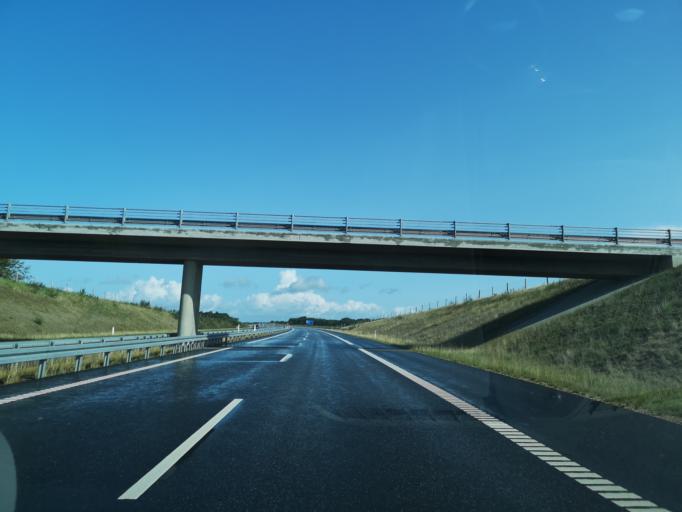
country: DK
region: Central Jutland
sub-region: Herning Kommune
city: Snejbjerg
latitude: 56.1744
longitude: 8.8923
